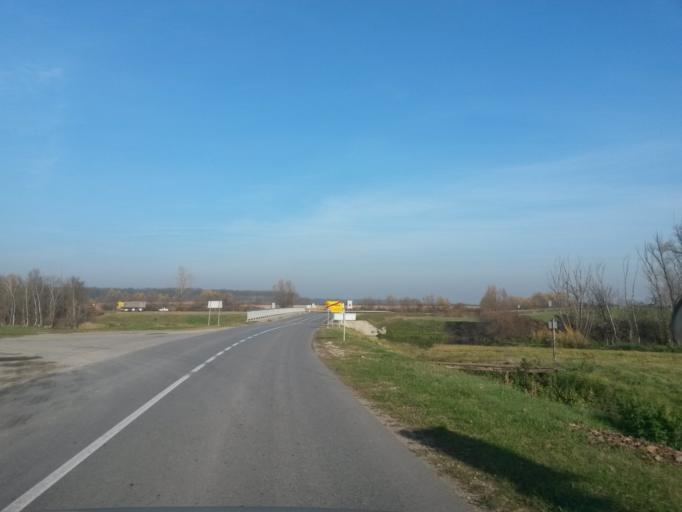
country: HR
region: Vukovarsko-Srijemska
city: Privlaka
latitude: 45.2119
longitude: 18.8577
